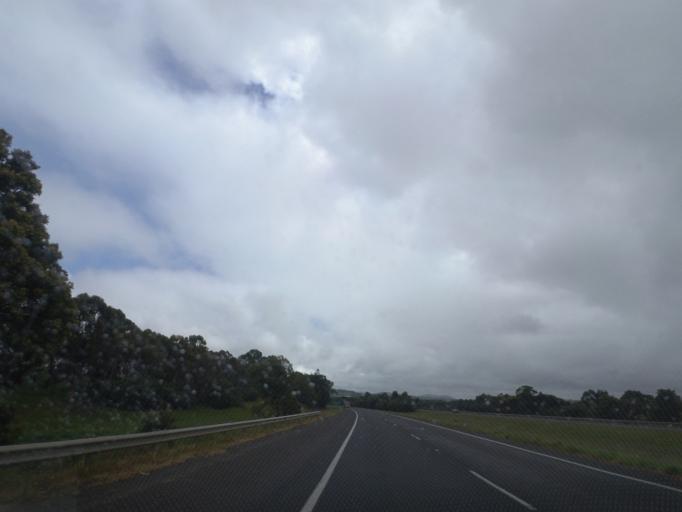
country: AU
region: Victoria
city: Black Hill
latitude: -37.5279
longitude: 143.8694
